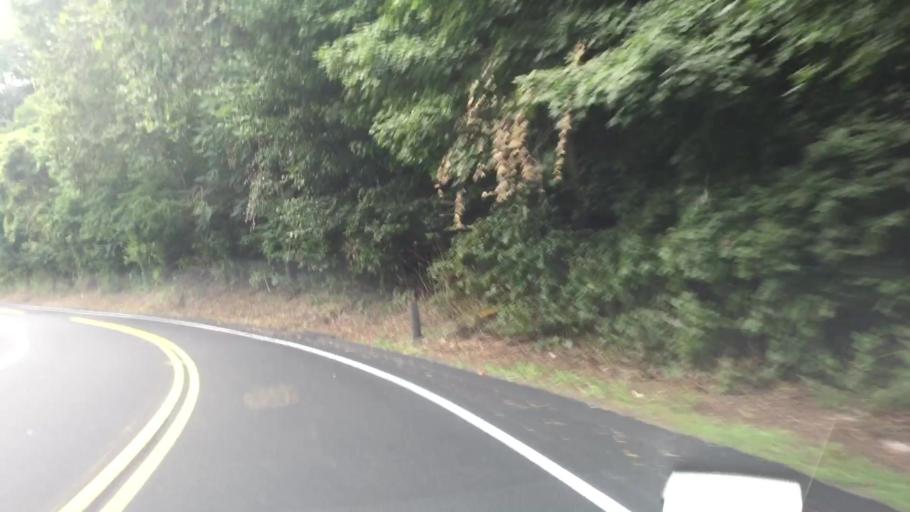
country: US
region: Pennsylvania
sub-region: Allegheny County
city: Carnegie
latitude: 40.4140
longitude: -80.0969
